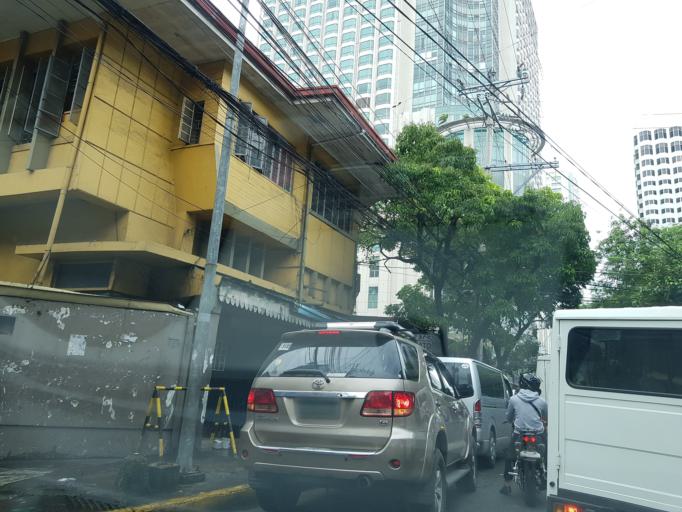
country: PH
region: Metro Manila
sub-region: City of Manila
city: Port Area
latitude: 14.5742
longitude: 120.9818
